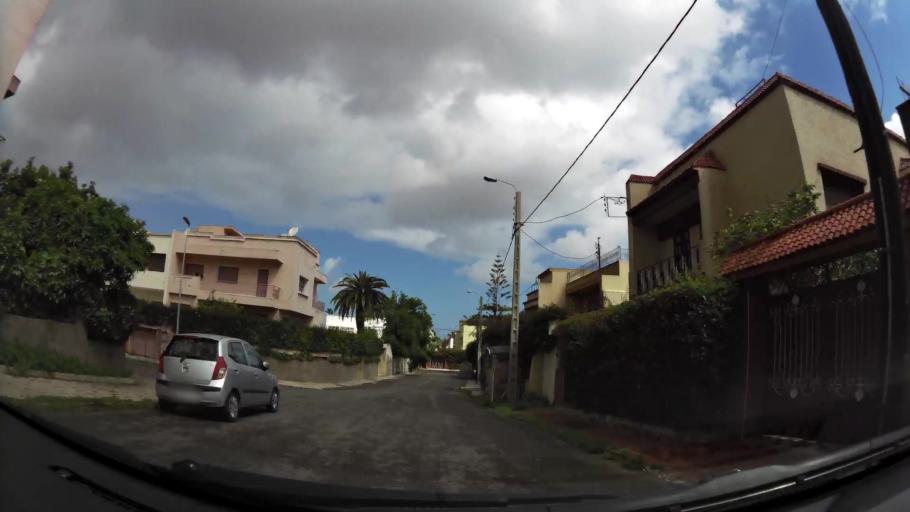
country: MA
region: Grand Casablanca
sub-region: Casablanca
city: Casablanca
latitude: 33.5537
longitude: -7.6093
